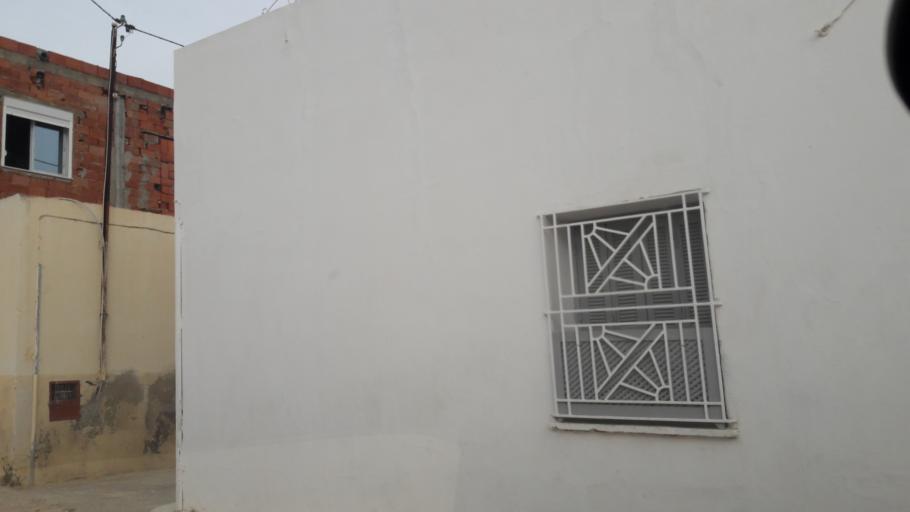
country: TN
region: Safaqis
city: Al Qarmadah
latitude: 34.7765
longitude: 10.7648
